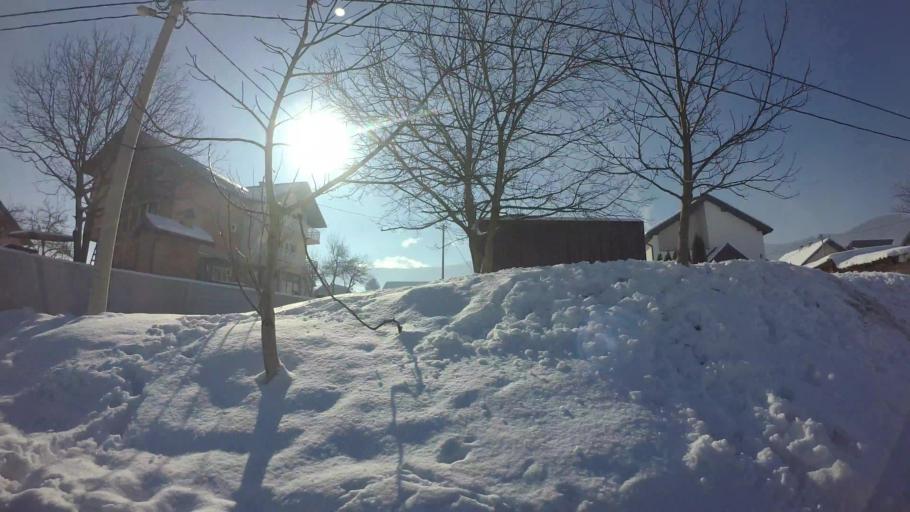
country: BA
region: Federation of Bosnia and Herzegovina
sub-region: Kanton Sarajevo
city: Sarajevo
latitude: 43.7996
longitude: 18.3425
